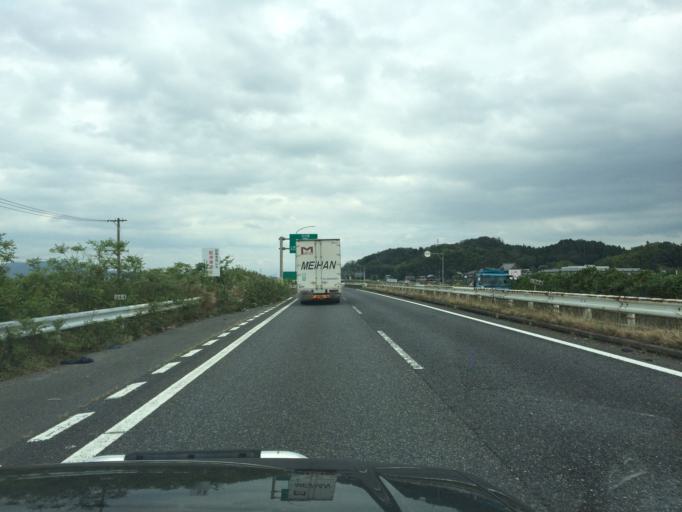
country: JP
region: Mie
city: Ueno-ebisumachi
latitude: 34.7438
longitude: 136.1176
